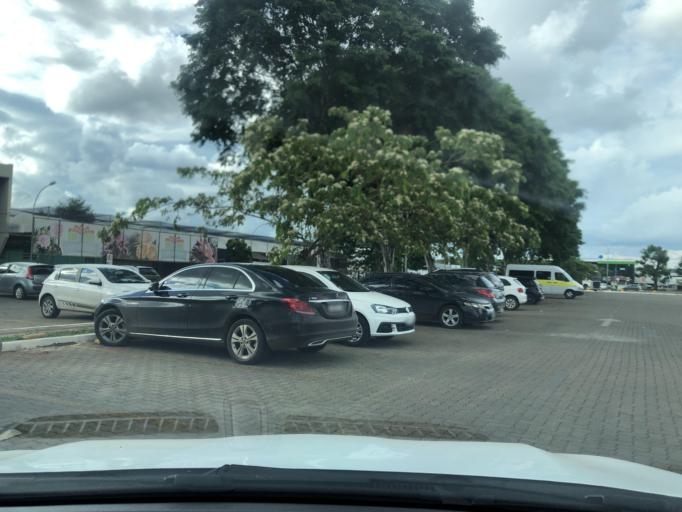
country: BR
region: Federal District
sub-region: Brasilia
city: Brasilia
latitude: -15.7942
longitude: -47.9493
